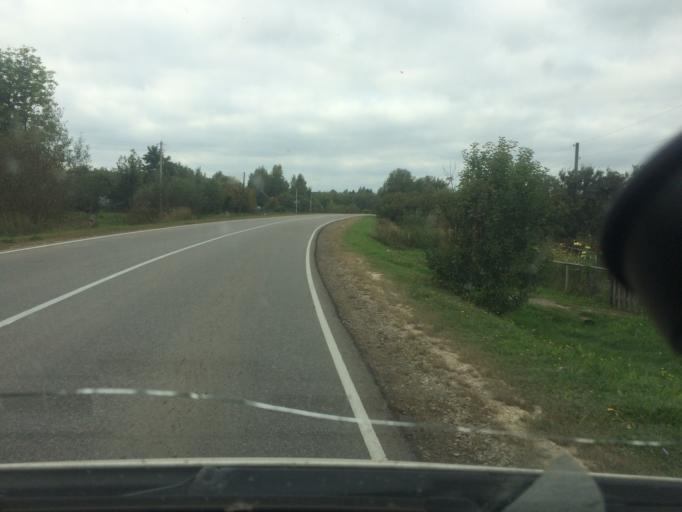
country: RU
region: Tula
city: Odoyev
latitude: 53.9989
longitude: 36.6697
